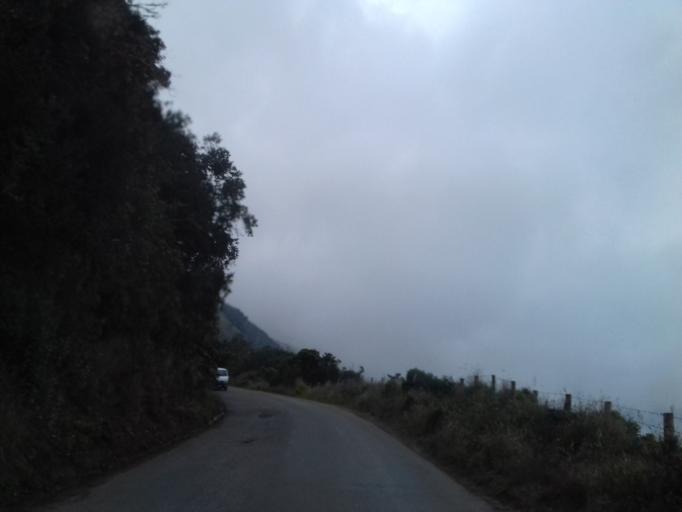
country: CO
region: Tolima
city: Herveo
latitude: 5.0111
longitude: -75.3304
